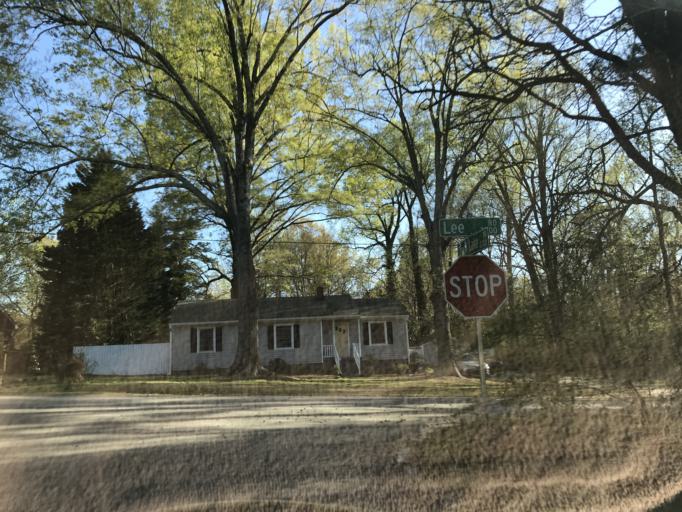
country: US
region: North Carolina
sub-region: Wake County
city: Raleigh
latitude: 35.8356
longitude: -78.5756
